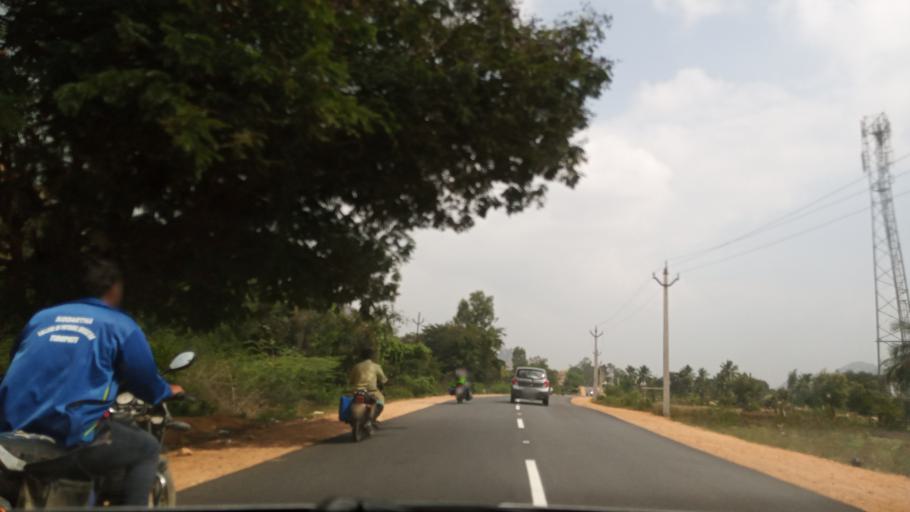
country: IN
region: Andhra Pradesh
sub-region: Chittoor
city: Madanapalle
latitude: 13.6367
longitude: 78.5930
